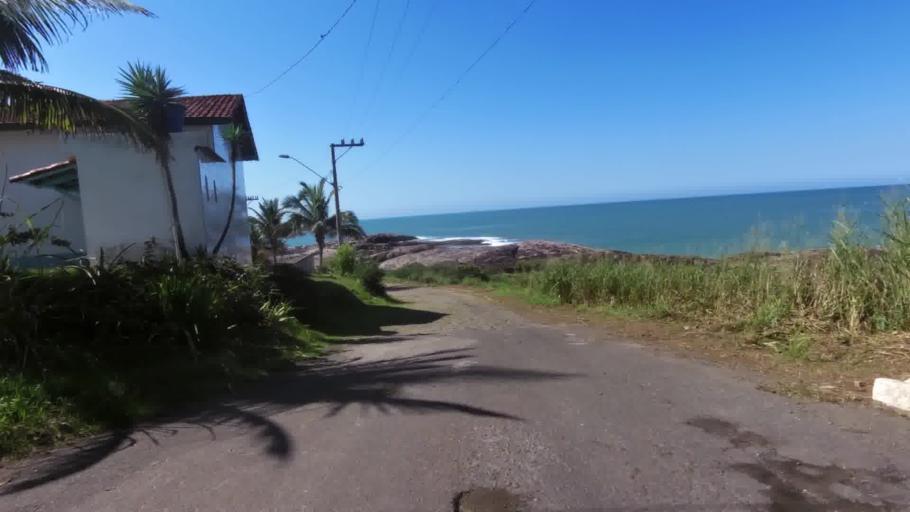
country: BR
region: Espirito Santo
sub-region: Guarapari
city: Guarapari
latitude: -20.7426
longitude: -40.5357
